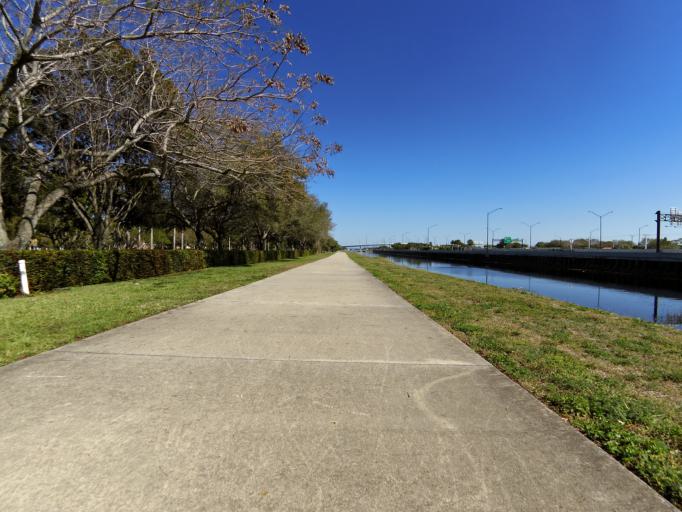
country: US
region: Florida
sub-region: Broward County
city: Pine Island Ridge
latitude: 26.1019
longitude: -80.2577
